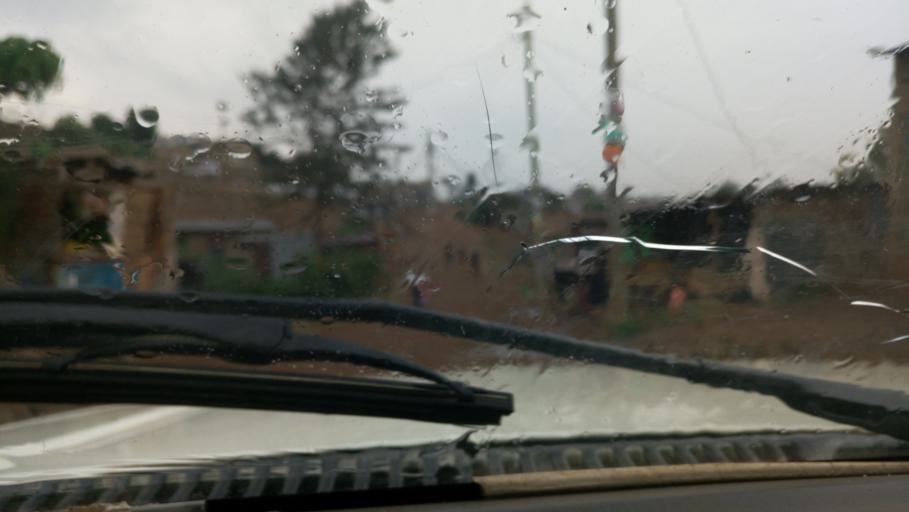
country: KE
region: Kiambu
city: Kiambu
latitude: -1.2009
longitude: 36.8846
